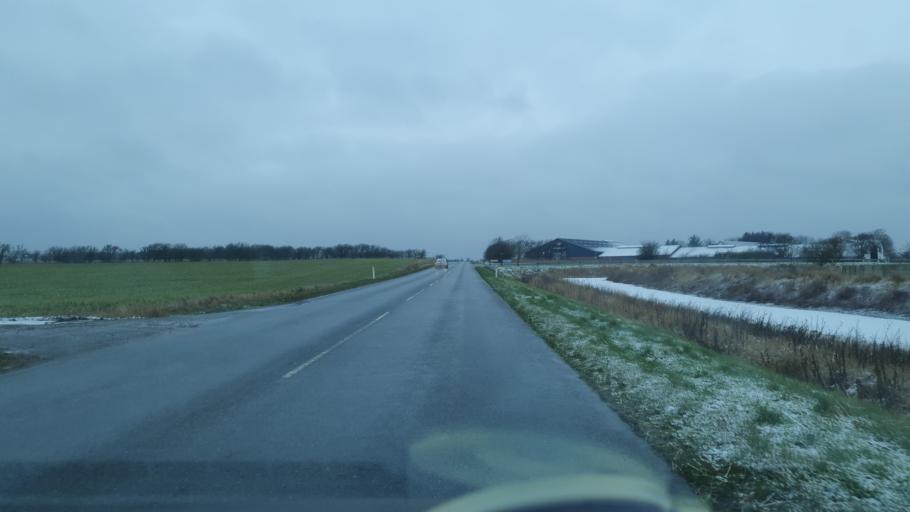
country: DK
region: North Denmark
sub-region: Jammerbugt Kommune
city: Brovst
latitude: 57.1217
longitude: 9.4930
